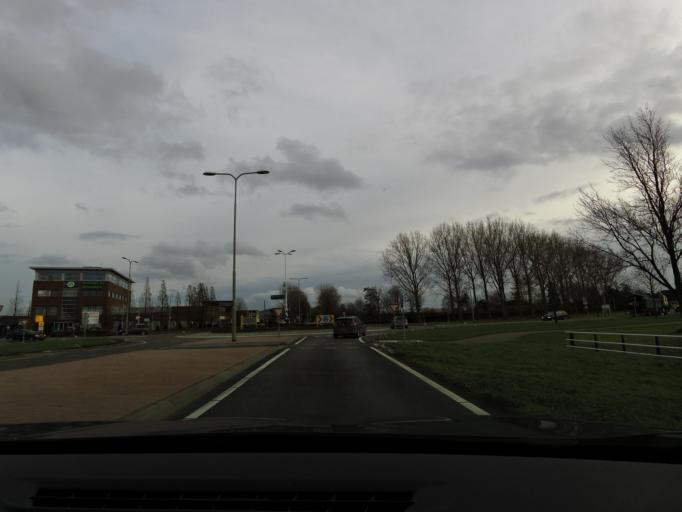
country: NL
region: North Brabant
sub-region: Gemeente Moerdijk
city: Willemstad
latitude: 51.7471
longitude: 4.4408
